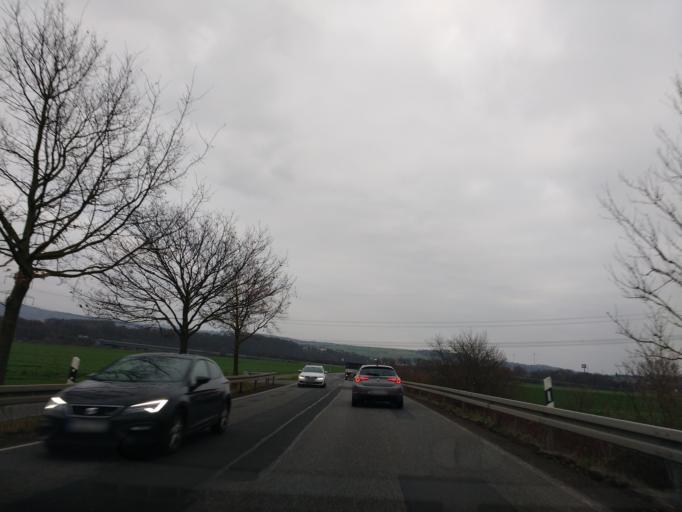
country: DE
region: Hesse
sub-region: Regierungsbezirk Kassel
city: Guxhagen
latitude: 51.2084
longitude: 9.4586
